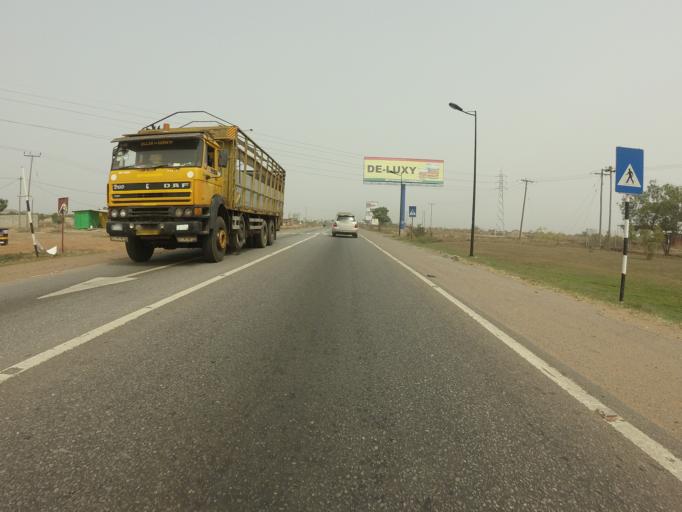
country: GH
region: Greater Accra
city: Tema
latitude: 5.7761
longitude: 0.0829
